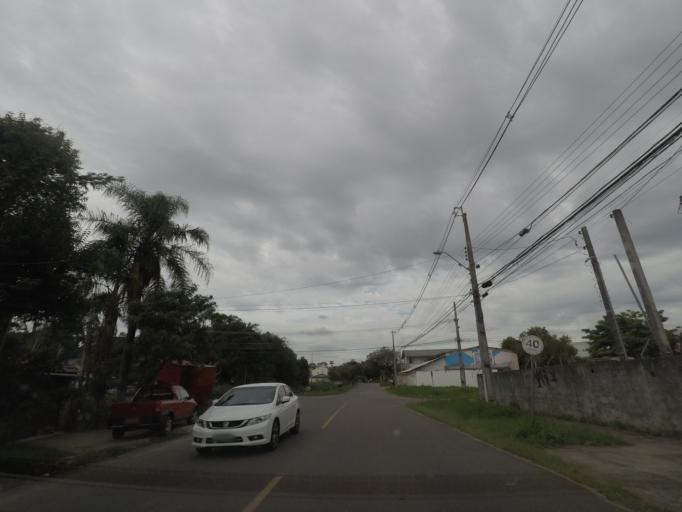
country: BR
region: Parana
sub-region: Pinhais
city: Pinhais
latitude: -25.4732
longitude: -49.2270
